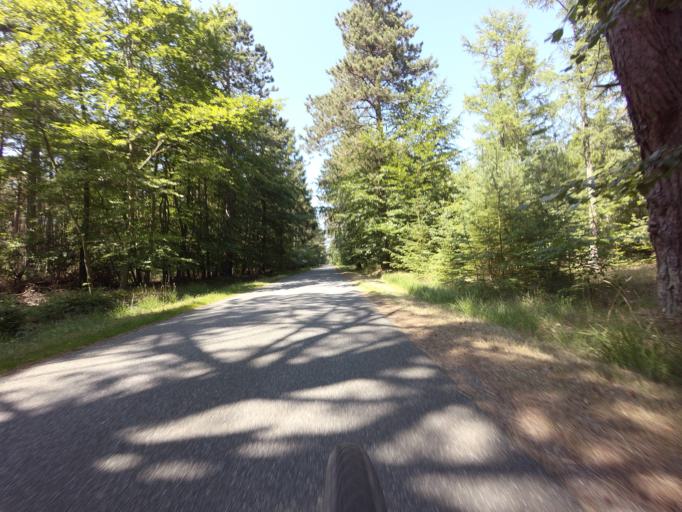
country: DK
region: North Denmark
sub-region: Laeso Kommune
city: Byrum
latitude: 57.2879
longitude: 11.0056
